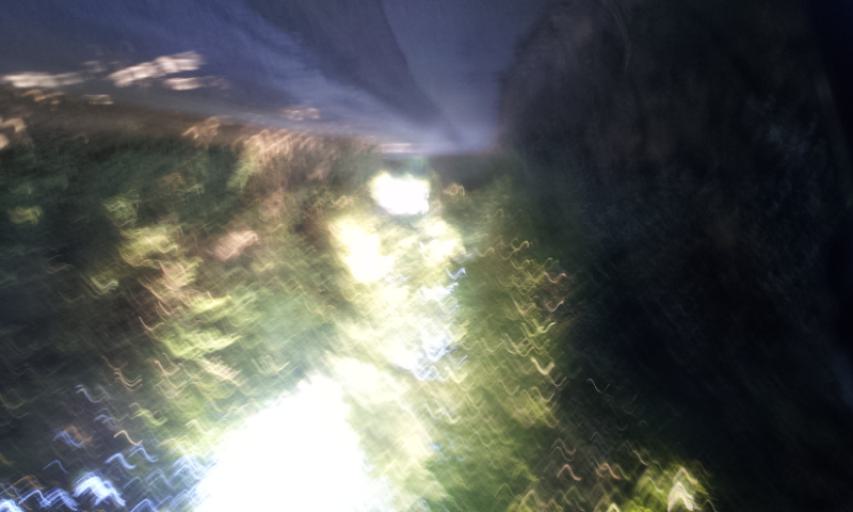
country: GB
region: England
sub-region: Kent
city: Yalding
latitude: 51.2296
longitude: 0.4764
